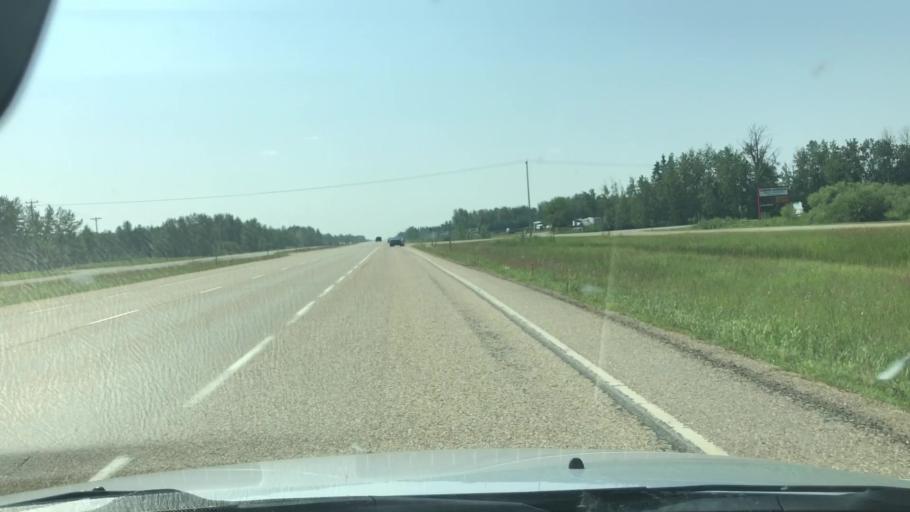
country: CA
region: Alberta
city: Devon
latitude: 53.4258
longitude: -113.7636
